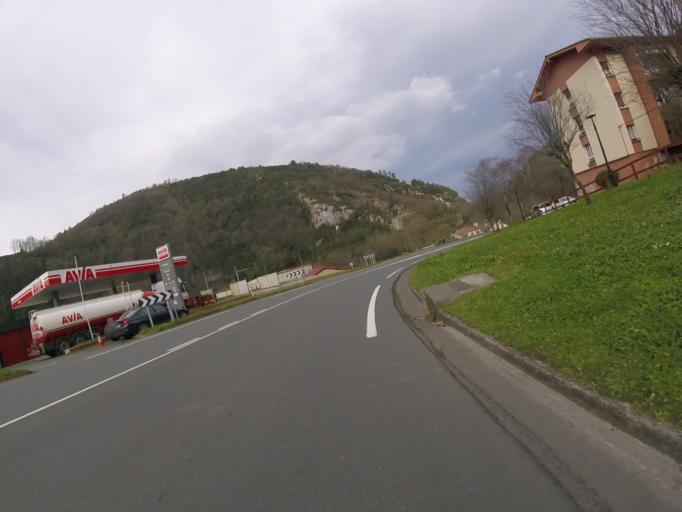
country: ES
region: Basque Country
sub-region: Provincia de Guipuzcoa
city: Cestona
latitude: 43.2414
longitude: -2.2590
